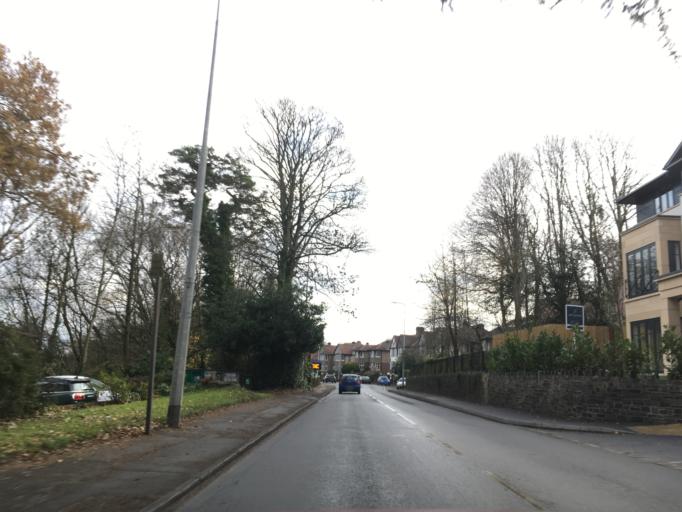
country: GB
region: Wales
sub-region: Cardiff
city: Cardiff
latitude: 51.4899
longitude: -3.2102
